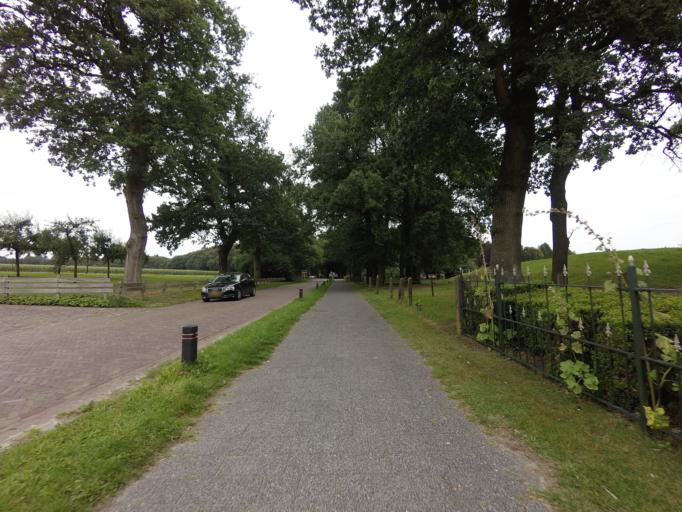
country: NL
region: Drenthe
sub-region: Gemeente Westerveld
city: Dwingeloo
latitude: 52.8602
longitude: 6.3211
